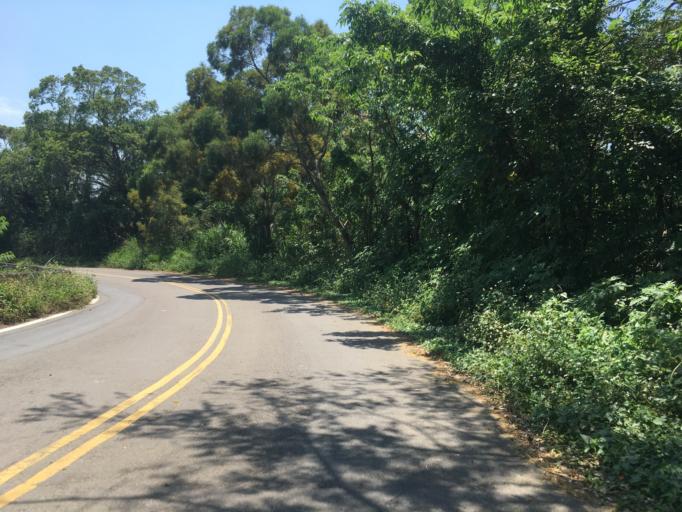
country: TW
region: Taiwan
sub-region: Hsinchu
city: Hsinchu
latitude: 24.7345
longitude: 120.9877
